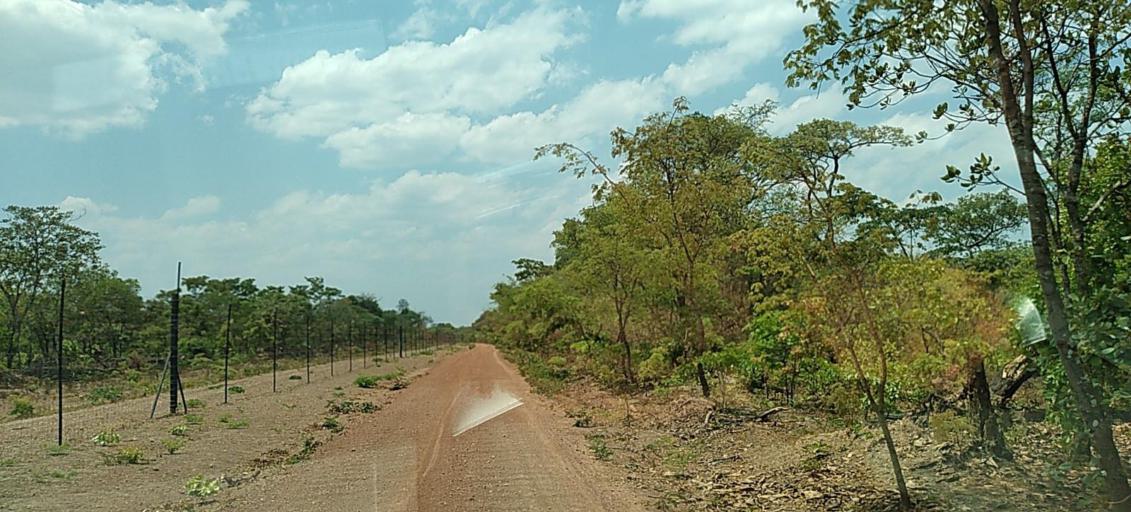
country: ZM
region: Copperbelt
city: Chililabombwe
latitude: -12.5202
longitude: 27.6258
